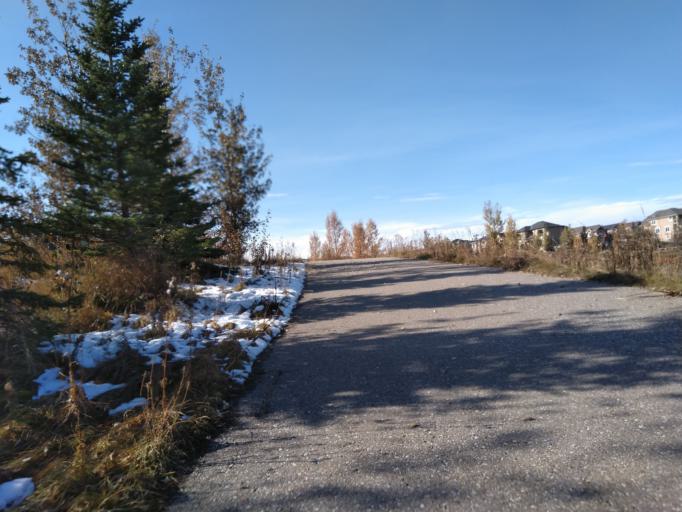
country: CA
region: Alberta
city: Calgary
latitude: 51.1704
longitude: -114.1281
